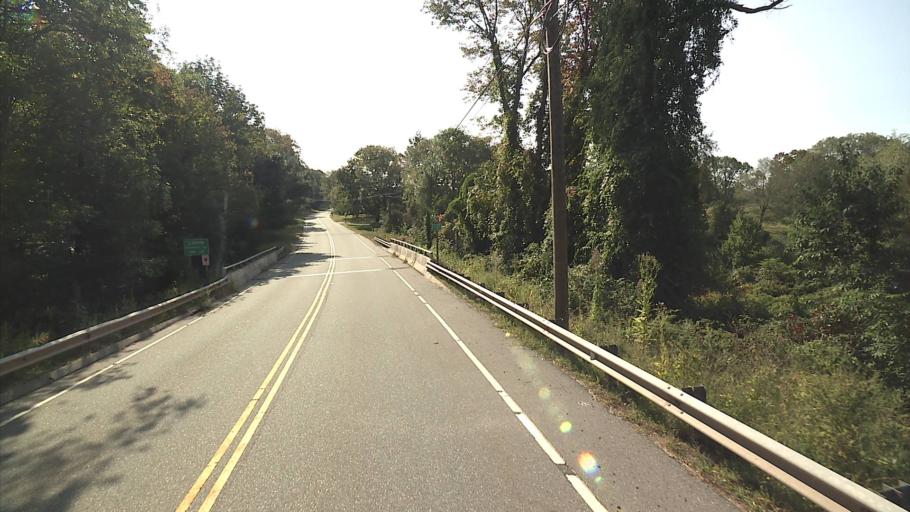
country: US
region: Connecticut
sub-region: Windham County
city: Willimantic
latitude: 41.6738
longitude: -72.2676
